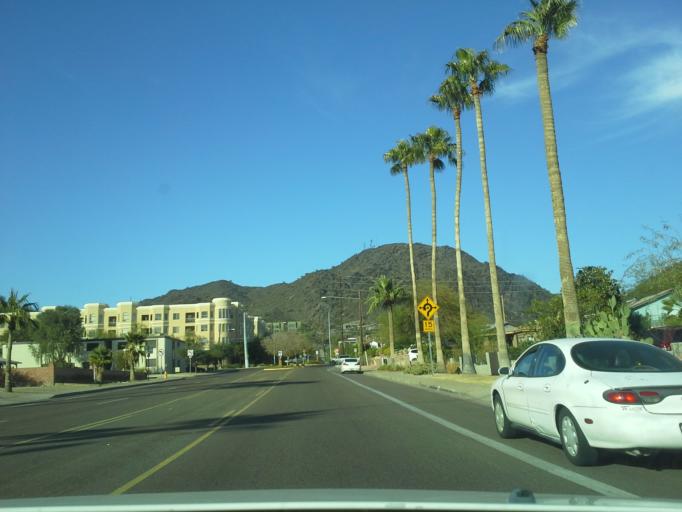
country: US
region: Arizona
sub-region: Maricopa County
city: Glendale
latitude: 33.5738
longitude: -112.0738
